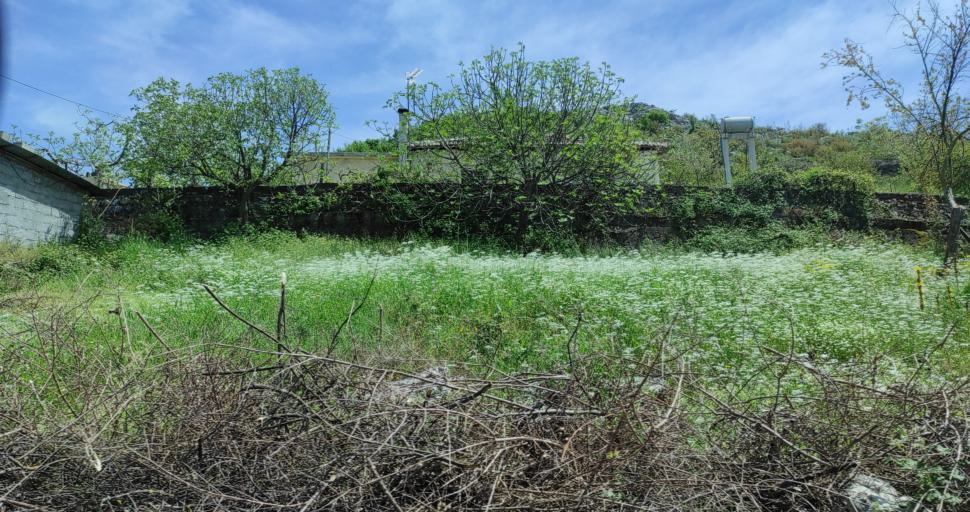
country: AL
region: Shkoder
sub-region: Rrethi i Malesia e Madhe
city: Gruemire
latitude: 42.1415
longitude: 19.5475
